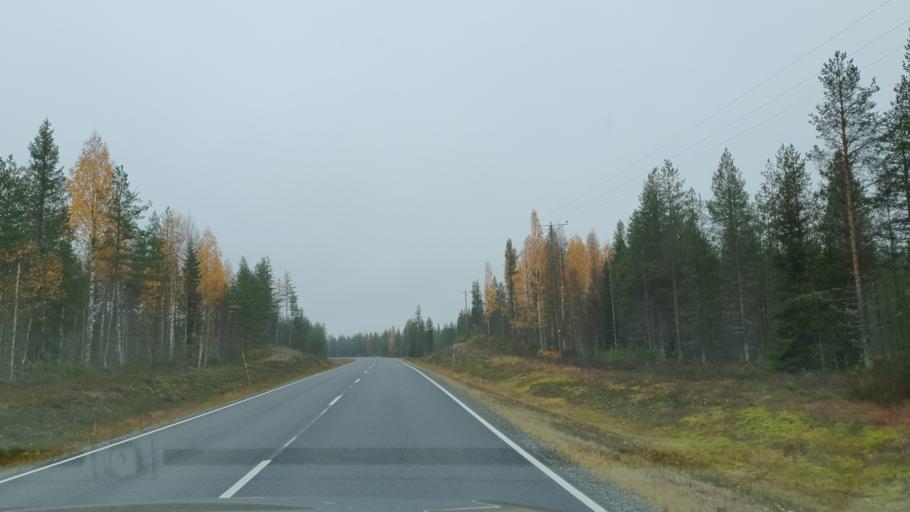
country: FI
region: Lapland
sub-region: Rovaniemi
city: Ranua
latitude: 66.1361
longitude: 26.2757
